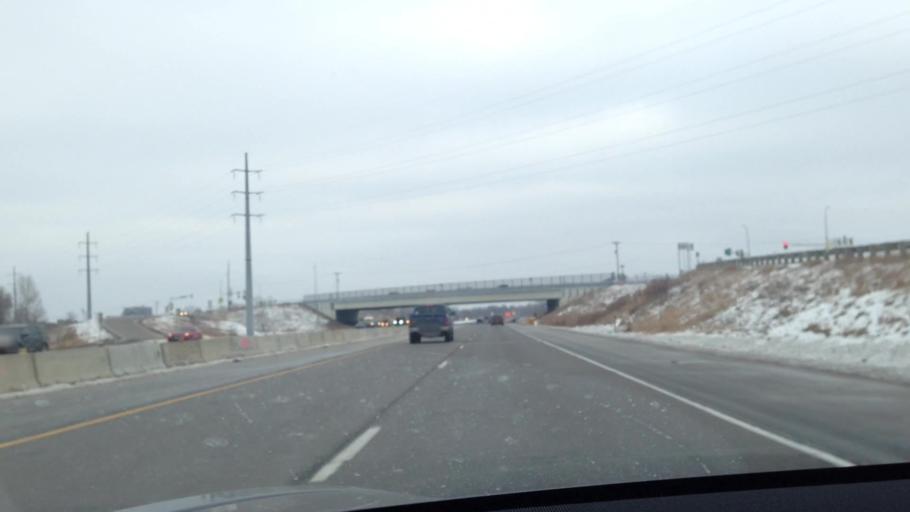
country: US
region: Minnesota
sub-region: Anoka County
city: Lexington
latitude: 45.1577
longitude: -93.1656
